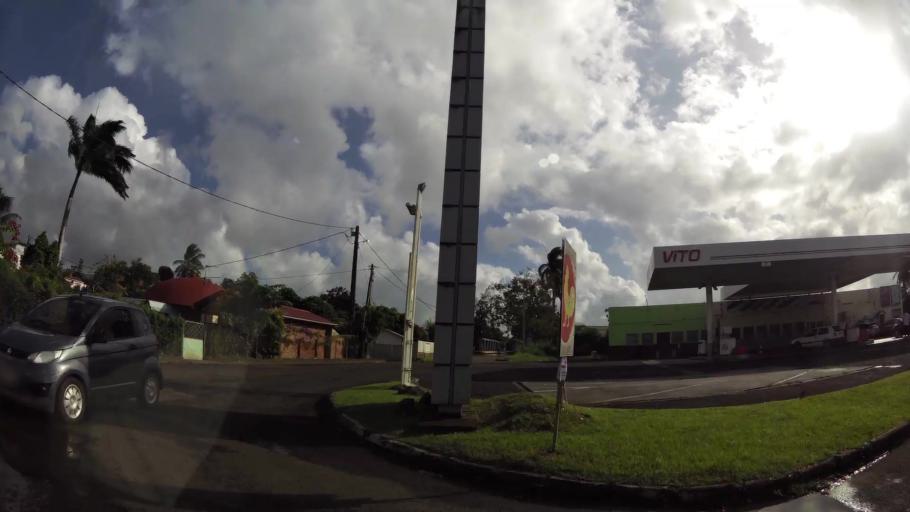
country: MQ
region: Martinique
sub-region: Martinique
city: Ducos
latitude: 14.5458
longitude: -60.9709
